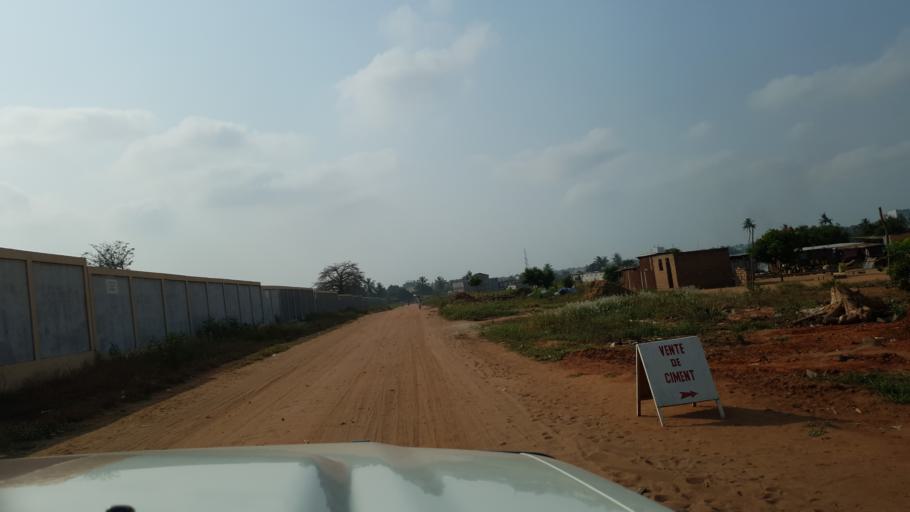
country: TG
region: Maritime
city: Lome
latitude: 6.1682
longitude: 1.2104
